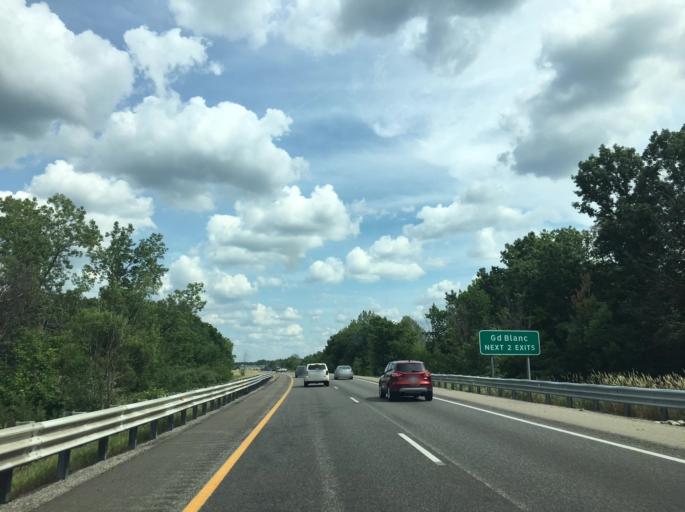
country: US
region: Michigan
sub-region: Genesee County
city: Grand Blanc
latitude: 42.9224
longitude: -83.6848
